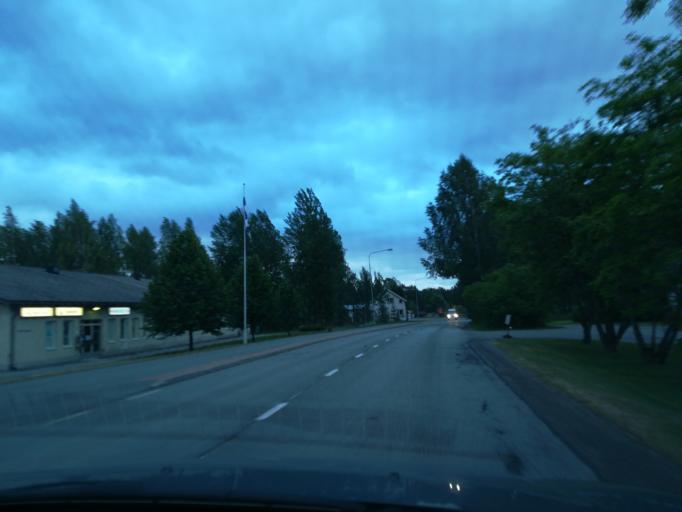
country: FI
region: Southern Savonia
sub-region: Mikkeli
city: Ristiina
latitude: 61.5076
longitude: 27.2548
